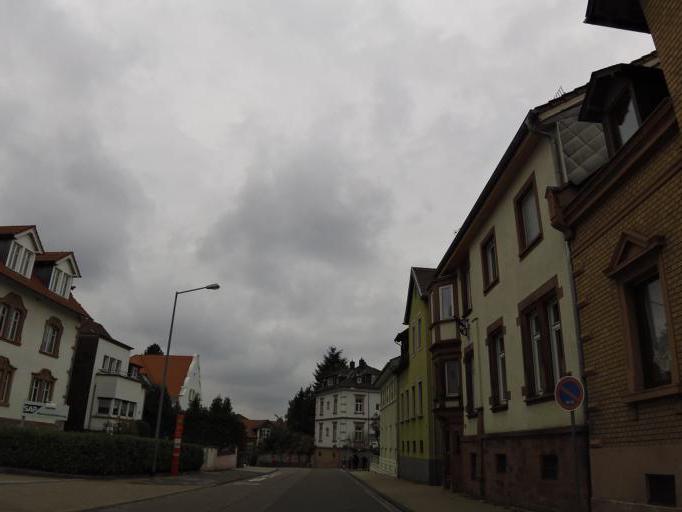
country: DE
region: Saarland
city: Sankt Ingbert
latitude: 49.2724
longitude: 7.1114
